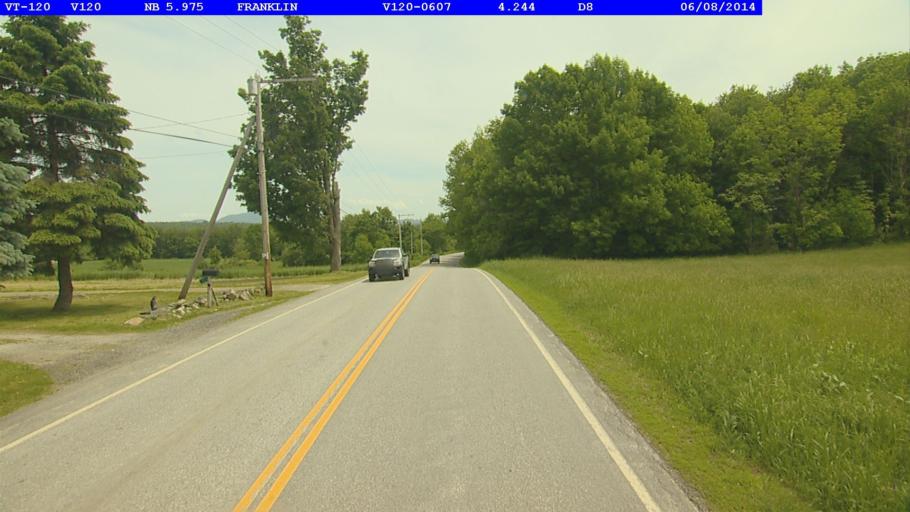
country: US
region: Vermont
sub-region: Franklin County
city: Enosburg Falls
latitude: 44.9870
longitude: -72.9086
